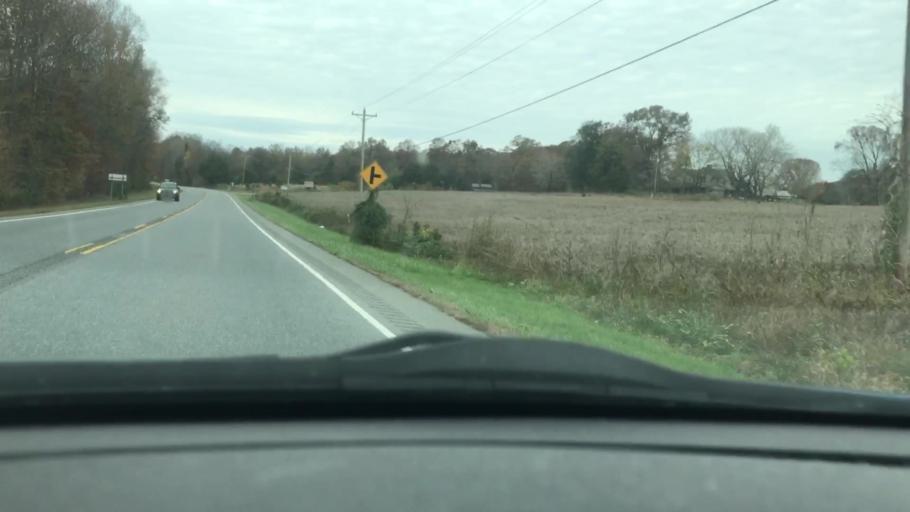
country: US
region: North Carolina
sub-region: Randolph County
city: Asheboro
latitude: 35.7305
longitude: -79.9423
